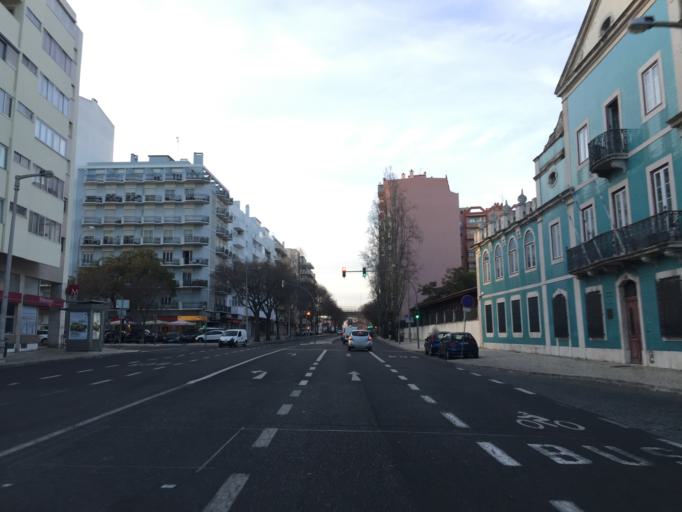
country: PT
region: Lisbon
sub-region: Odivelas
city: Olival do Basto
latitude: 38.7702
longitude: -9.1597
